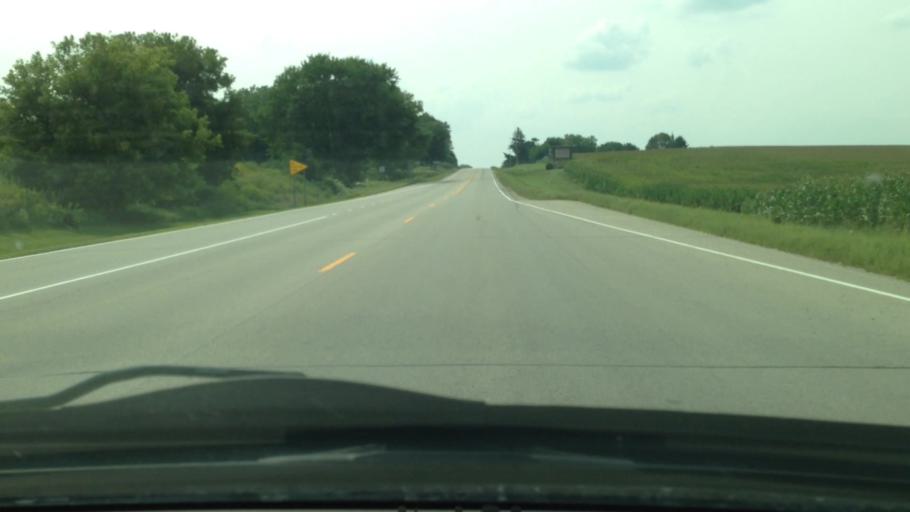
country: US
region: Minnesota
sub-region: Wabasha County
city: Plainview
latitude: 44.1650
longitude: -92.1839
